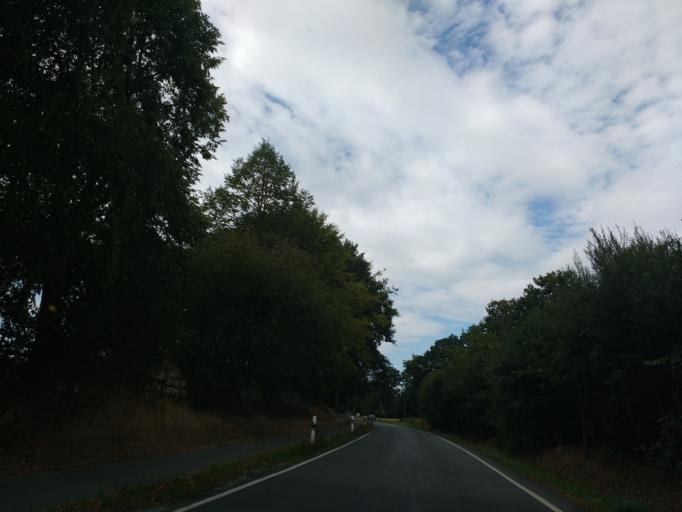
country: DE
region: North Rhine-Westphalia
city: Rietberg
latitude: 51.8162
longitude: 8.4490
